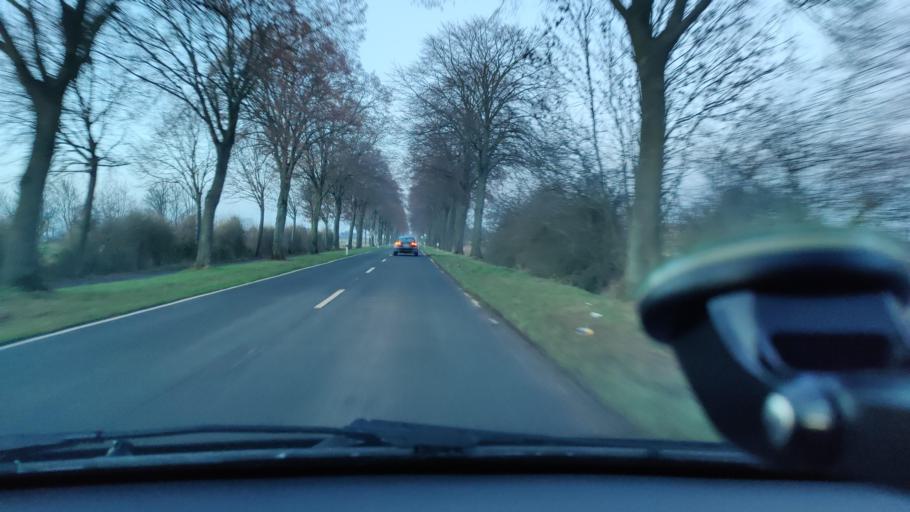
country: DE
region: North Rhine-Westphalia
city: Rheinberg
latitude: 51.5885
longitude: 6.6108
